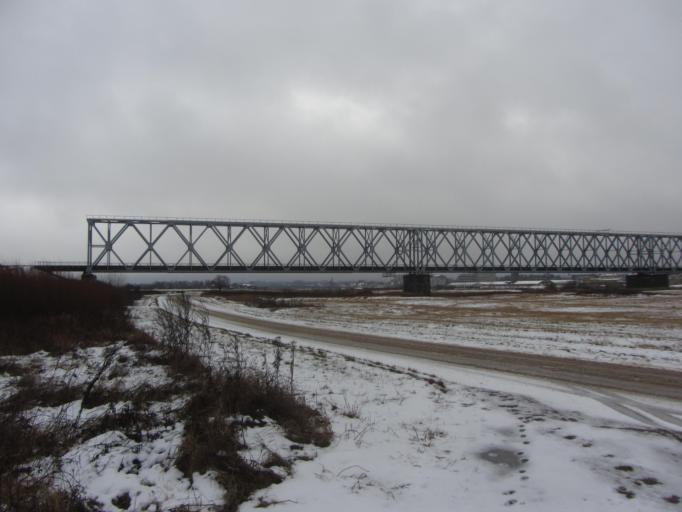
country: RU
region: Kaliningrad
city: Sovetsk
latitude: 55.0947
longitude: 21.8842
